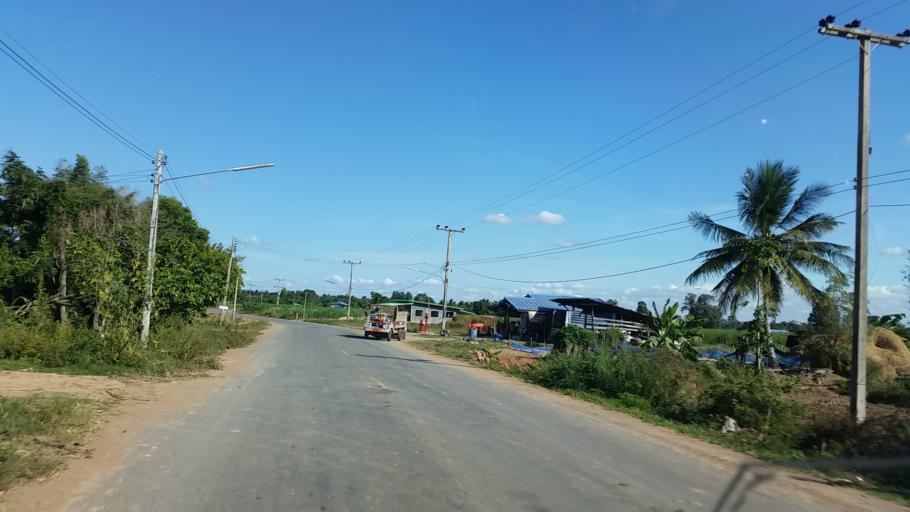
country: TH
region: Chaiyaphum
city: Thep Sathit
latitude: 15.5464
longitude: 101.4712
